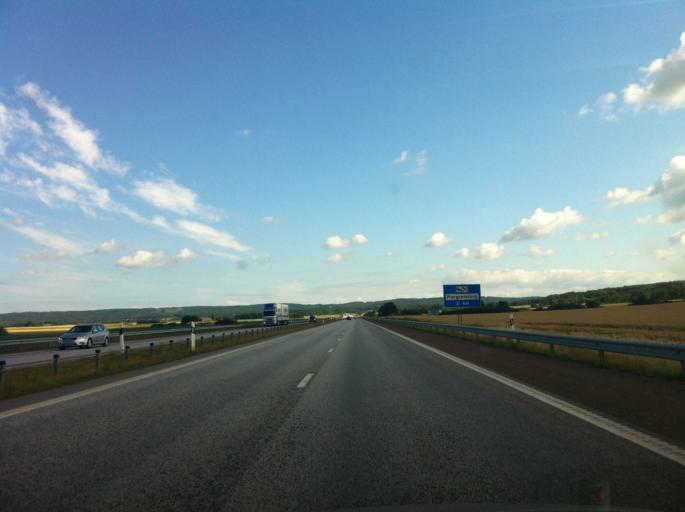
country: SE
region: Skane
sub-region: Angelholms Kommun
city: AEngelholm
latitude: 56.2926
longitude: 12.9032
